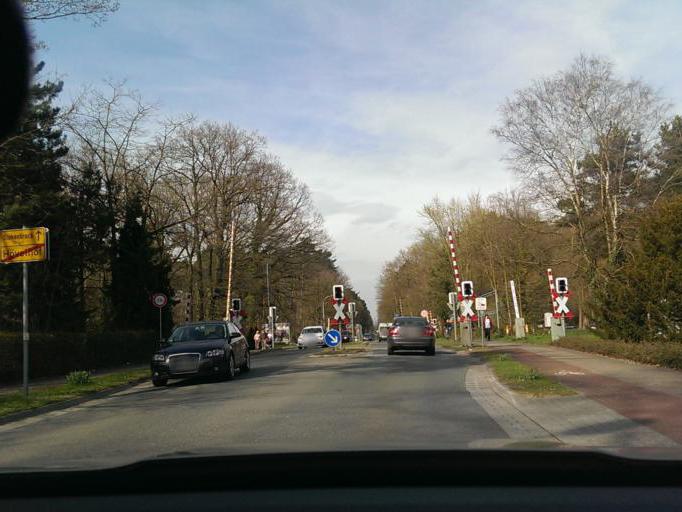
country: DE
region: North Rhine-Westphalia
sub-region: Regierungsbezirk Detmold
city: Hovelhof
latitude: 51.8280
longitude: 8.6564
